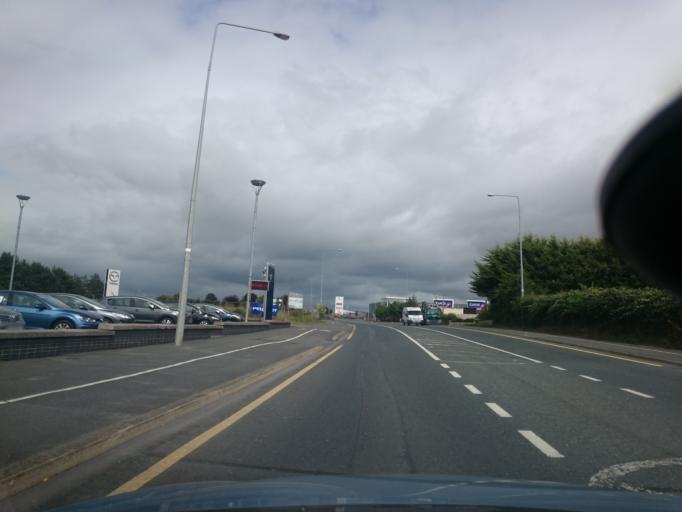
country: IE
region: Leinster
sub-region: County Carlow
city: Carlow
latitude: 52.8464
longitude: -6.9050
